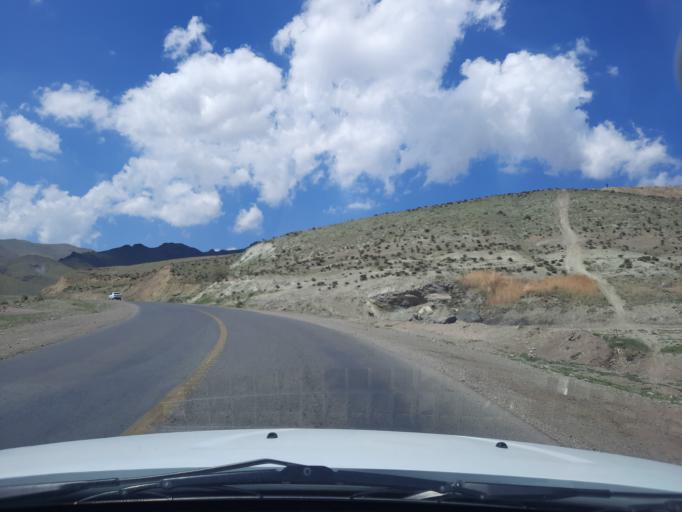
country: IR
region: Qazvin
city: Qazvin
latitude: 36.3534
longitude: 50.1894
